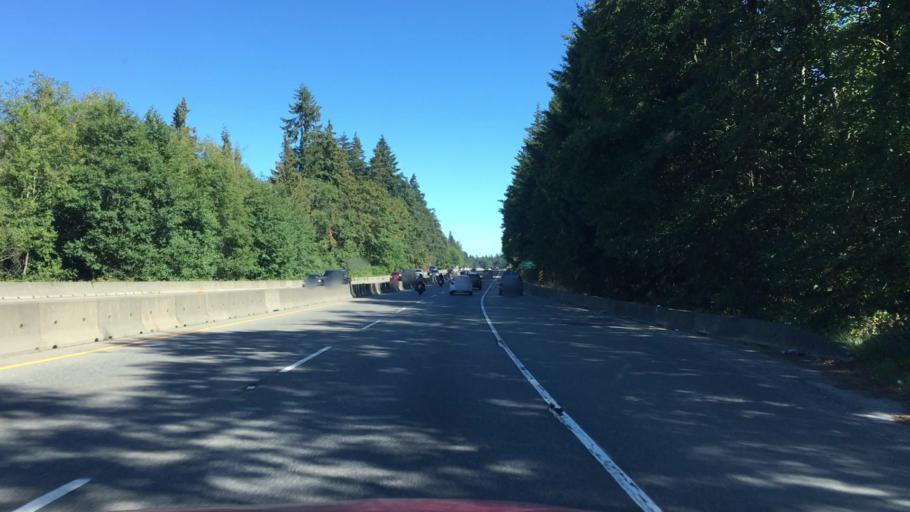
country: CA
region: British Columbia
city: Nanaimo
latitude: 49.2498
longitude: -124.0961
